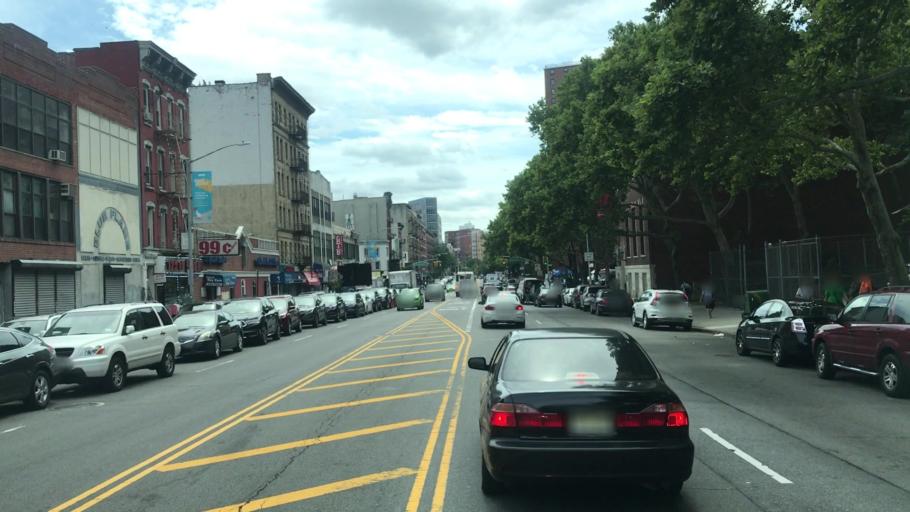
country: US
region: New Jersey
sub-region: Bergen County
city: Edgewater
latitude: 40.8145
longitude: -73.9573
